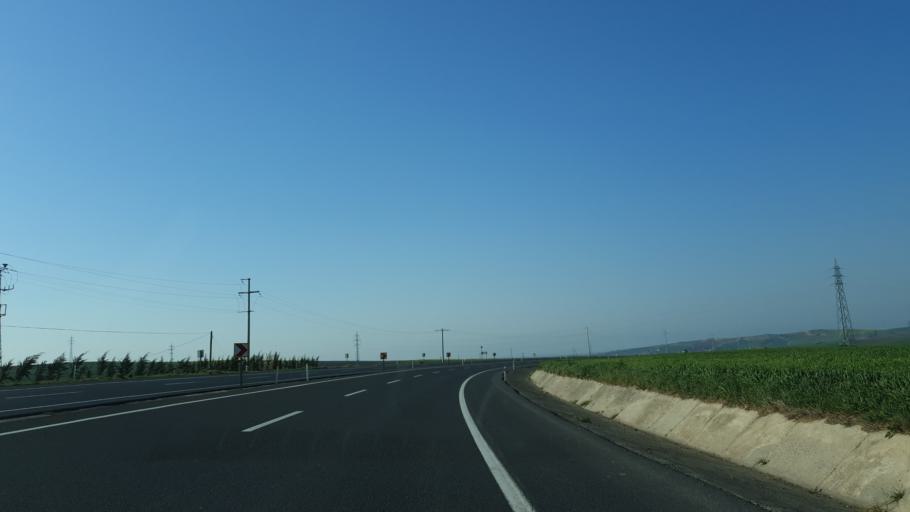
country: TR
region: Tekirdag
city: Corlu
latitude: 41.1008
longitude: 27.7544
